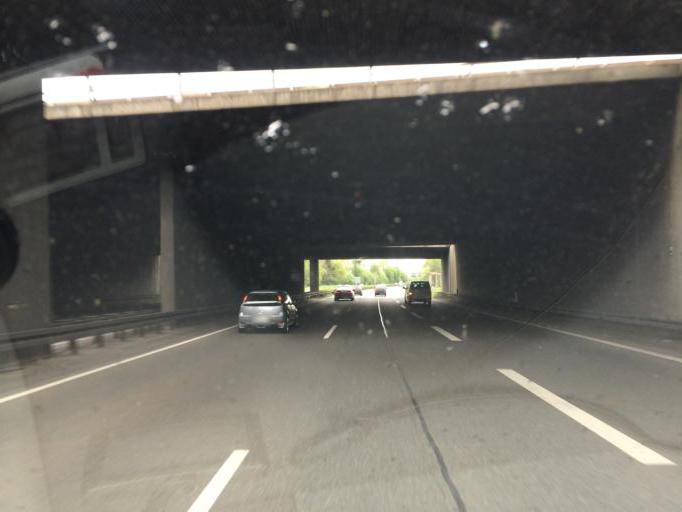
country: DE
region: North Rhine-Westphalia
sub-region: Regierungsbezirk Arnsberg
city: Herne
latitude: 51.5441
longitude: 7.2003
